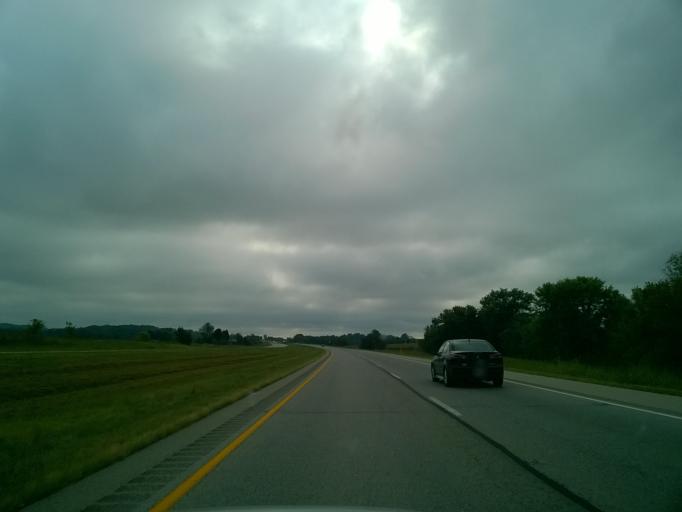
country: US
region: Indiana
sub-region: Harrison County
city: Corydon
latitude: 38.2412
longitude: -86.1892
